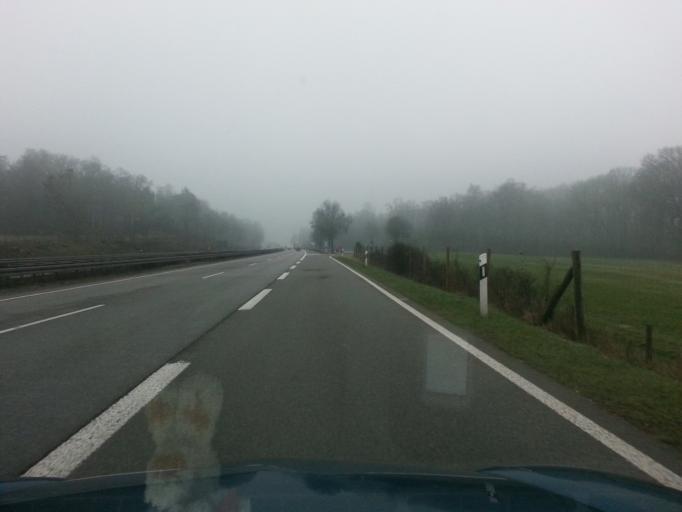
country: DE
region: North Rhine-Westphalia
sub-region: Regierungsbezirk Dusseldorf
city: Emmerich
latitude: 51.8753
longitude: 6.1933
